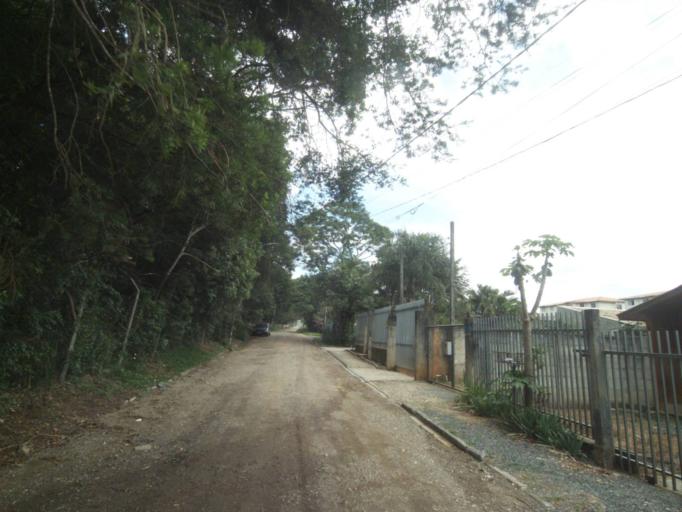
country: BR
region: Parana
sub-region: Curitiba
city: Curitiba
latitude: -25.4681
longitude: -49.3388
